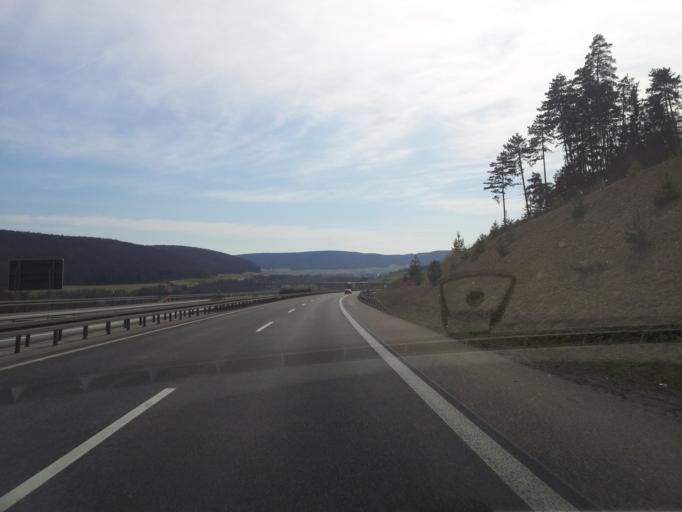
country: DE
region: Thuringia
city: Ellingshausen
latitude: 50.5680
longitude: 10.4799
